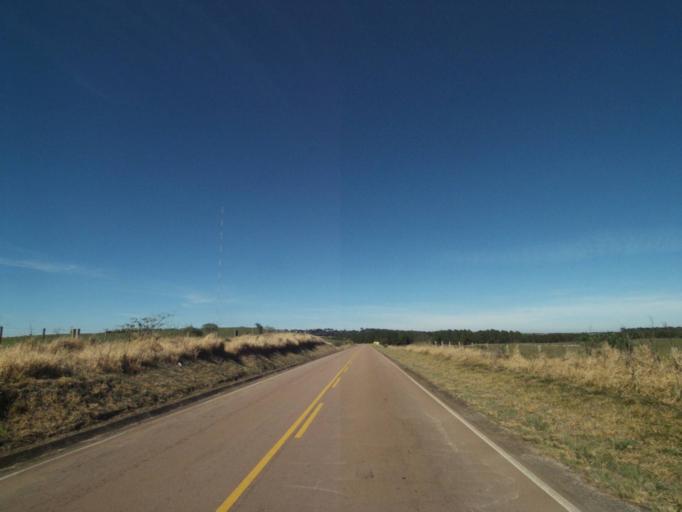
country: BR
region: Parana
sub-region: Tibagi
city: Tibagi
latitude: -24.6455
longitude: -50.2323
